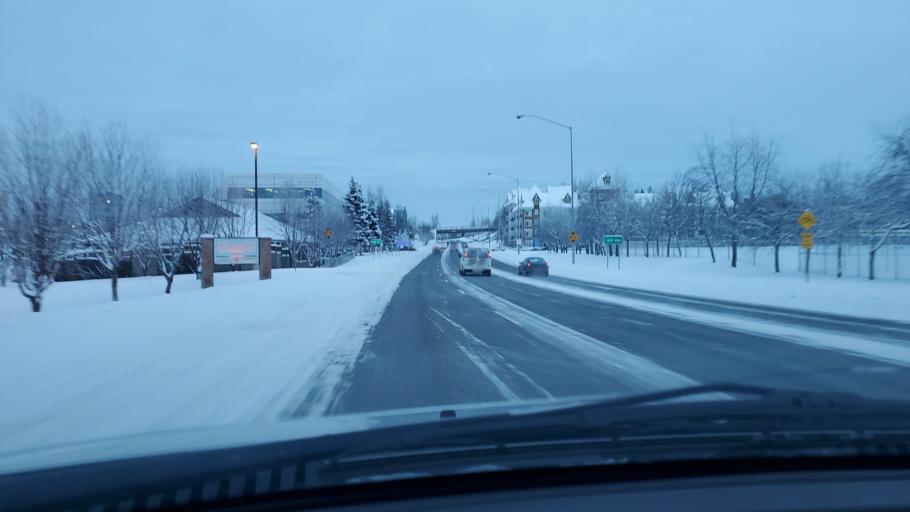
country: US
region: Alaska
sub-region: Anchorage Municipality
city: Anchorage
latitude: 61.2043
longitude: -149.8834
